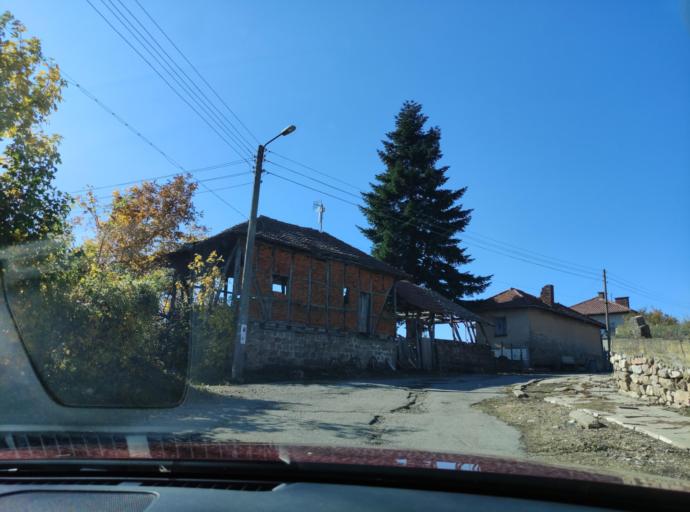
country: BG
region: Montana
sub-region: Obshtina Chiprovtsi
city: Chiprovtsi
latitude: 43.4547
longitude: 23.0325
